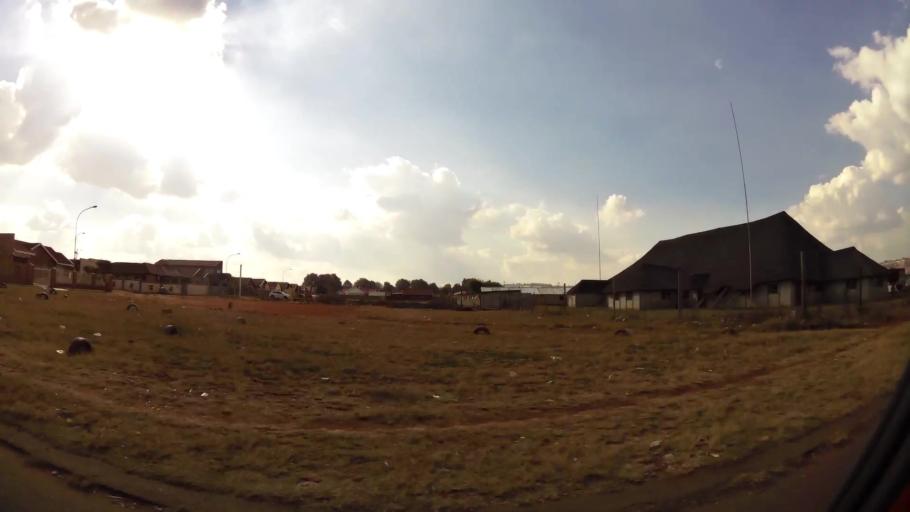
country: ZA
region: Gauteng
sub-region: City of Johannesburg Metropolitan Municipality
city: Roodepoort
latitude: -26.2136
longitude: 27.8666
